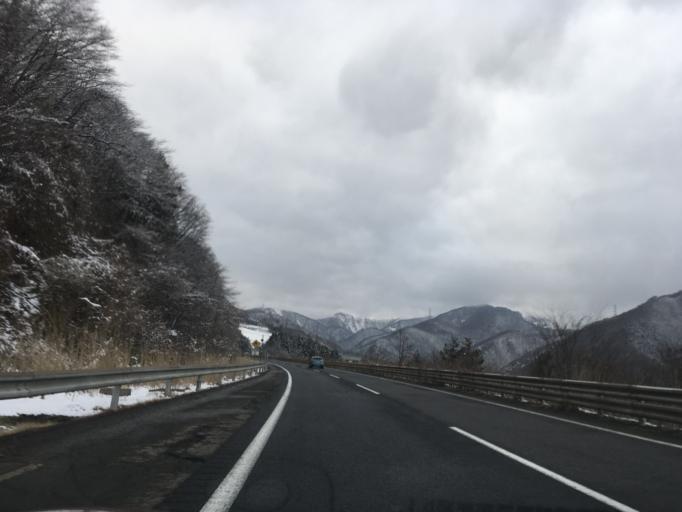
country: JP
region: Yamagata
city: Yamagata-shi
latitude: 38.2144
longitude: 140.5283
